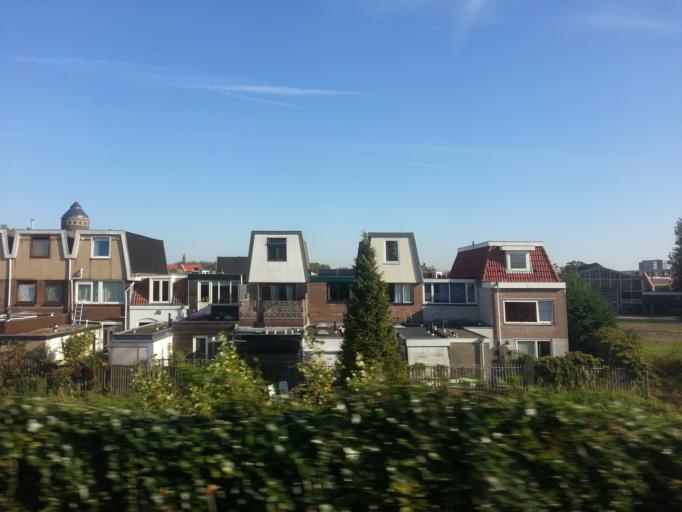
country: NL
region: Utrecht
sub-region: Gemeente Utrecht
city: Utrecht
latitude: 52.1010
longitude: 5.0934
